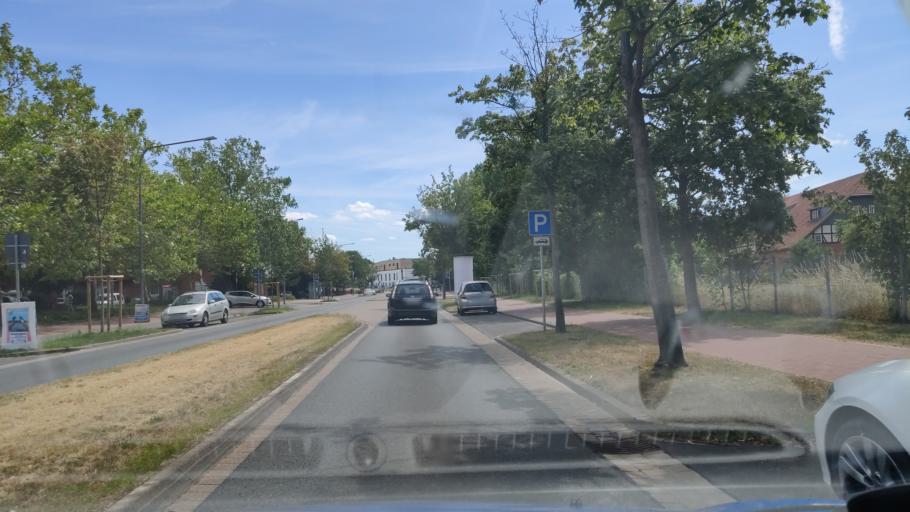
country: DE
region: Lower Saxony
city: Ronnenberg
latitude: 52.3408
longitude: 9.6674
